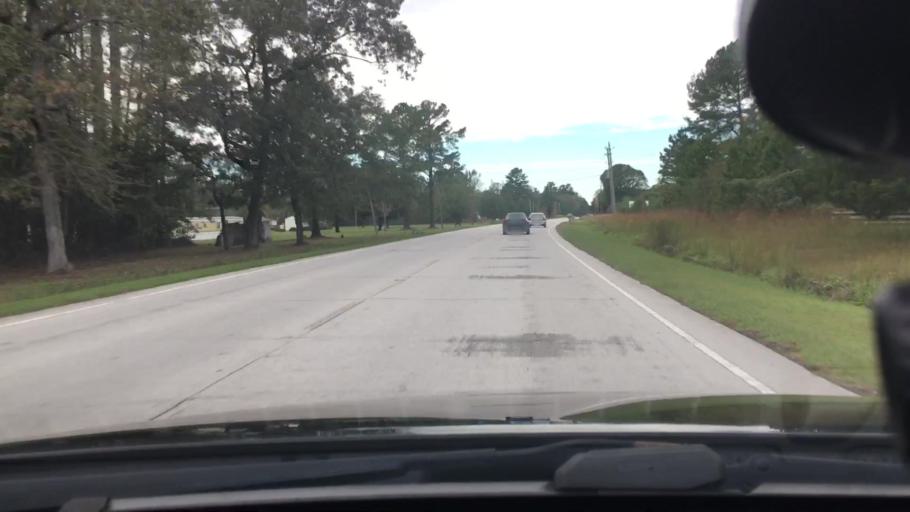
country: US
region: North Carolina
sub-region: Craven County
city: Vanceboro
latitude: 35.3841
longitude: -77.2257
